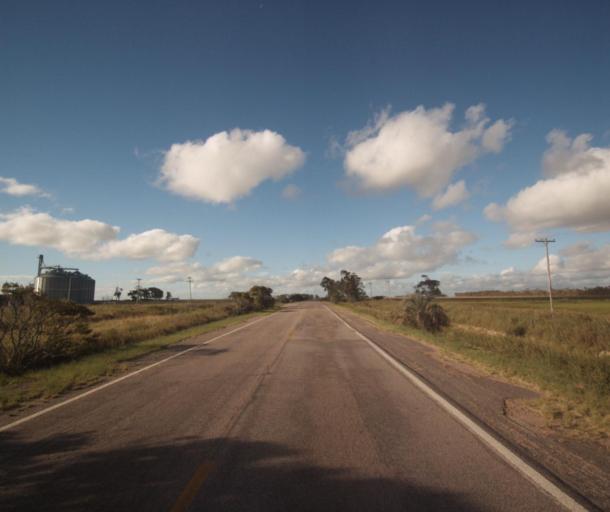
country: BR
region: Rio Grande do Sul
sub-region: Arroio Grande
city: Arroio Grande
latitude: -32.4459
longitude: -52.5693
